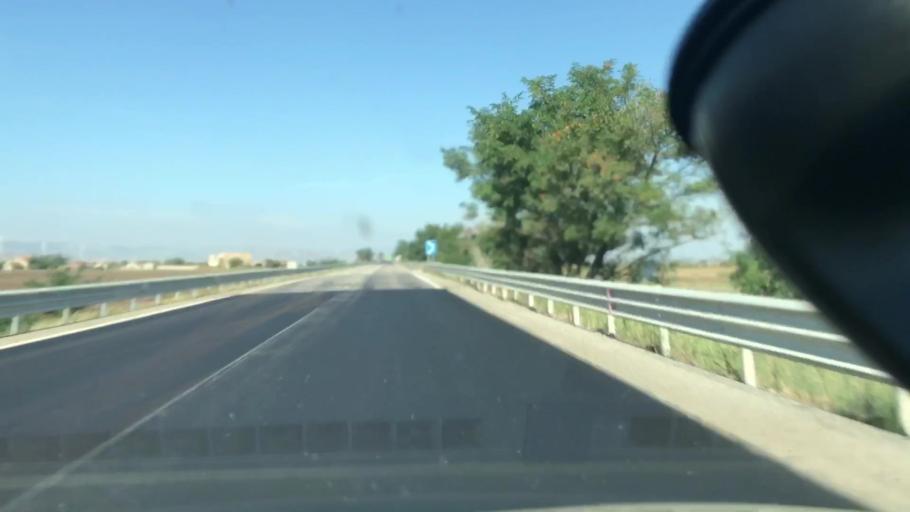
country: IT
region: Basilicate
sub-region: Provincia di Potenza
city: Zona 179
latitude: 41.0727
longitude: 15.6500
